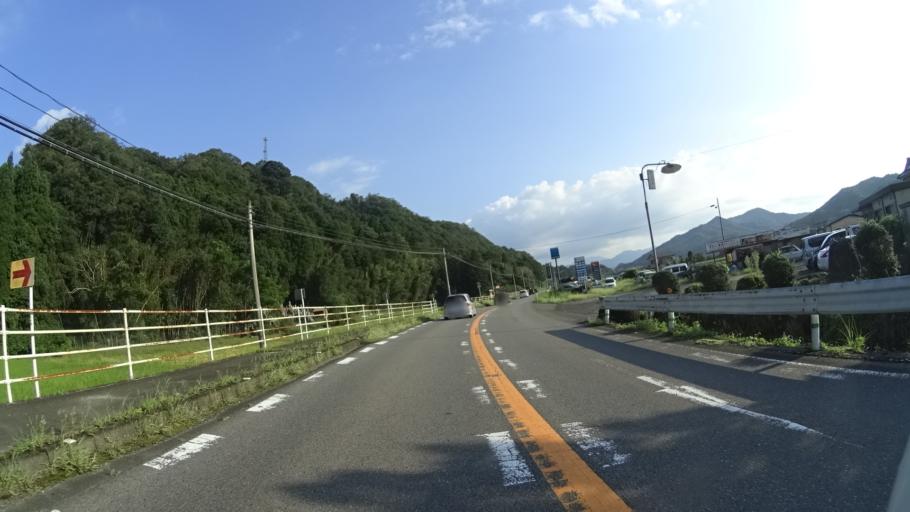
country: JP
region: Oita
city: Bungo-Takada-shi
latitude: 33.4644
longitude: 131.3308
